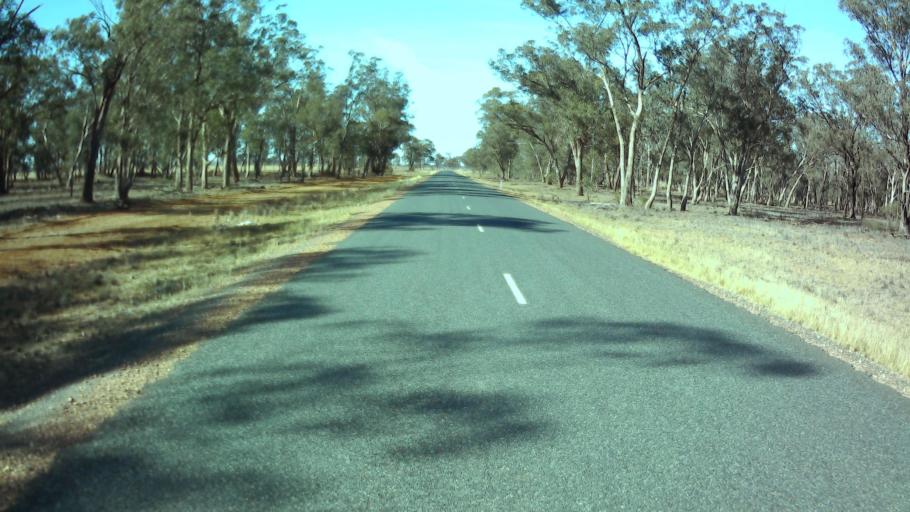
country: AU
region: New South Wales
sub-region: Weddin
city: Grenfell
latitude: -34.0654
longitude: 147.9072
